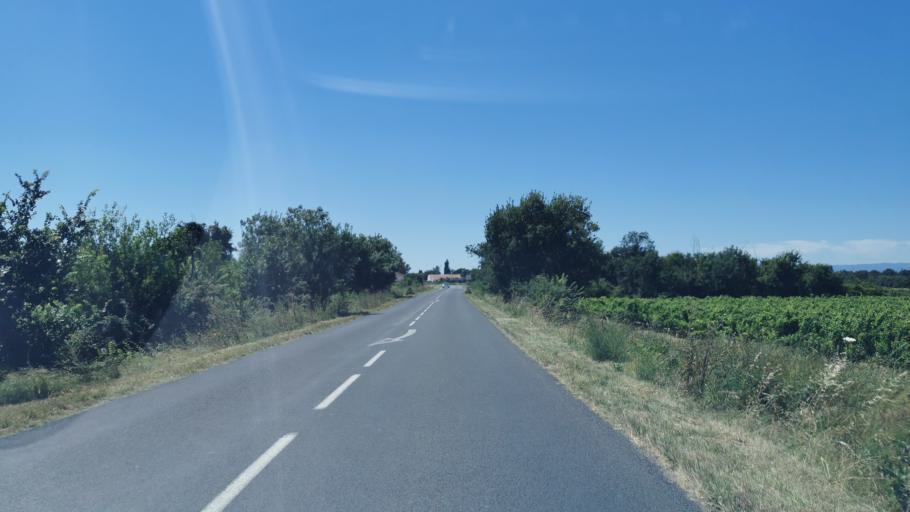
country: FR
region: Languedoc-Roussillon
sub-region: Departement de l'Aude
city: Coursan
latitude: 43.2329
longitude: 3.0805
